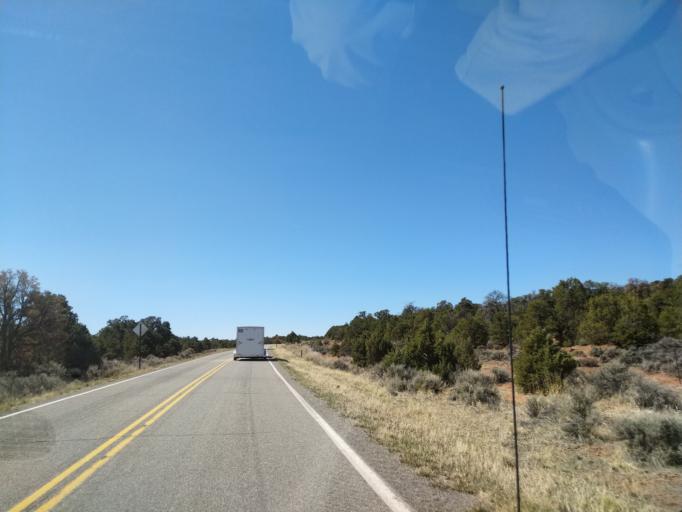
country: US
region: Colorado
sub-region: Mesa County
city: Redlands
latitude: 39.0124
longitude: -108.6722
